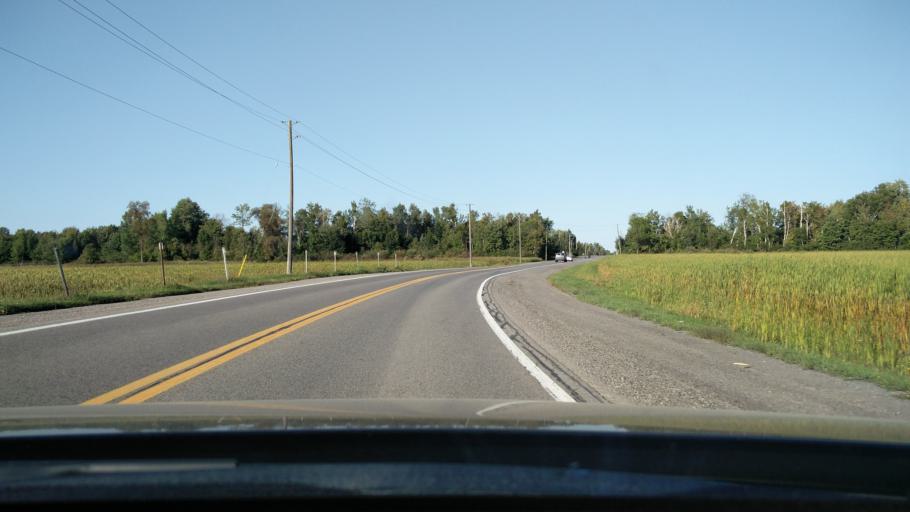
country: CA
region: Ontario
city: Carleton Place
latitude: 45.1107
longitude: -75.9722
